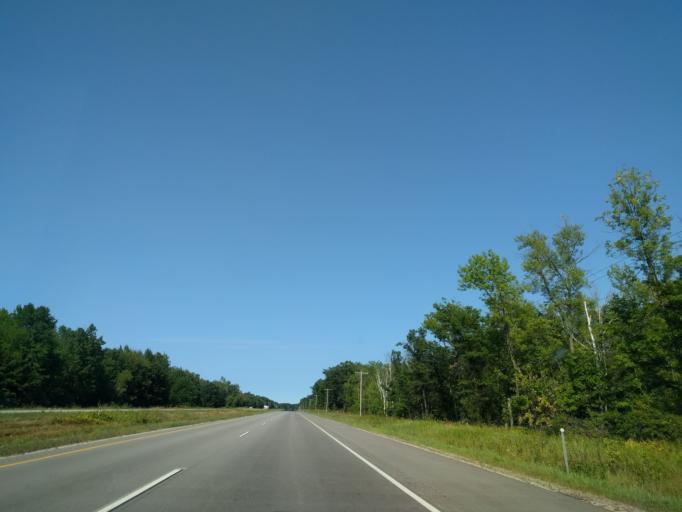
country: US
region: Wisconsin
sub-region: Oconto County
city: Oconto
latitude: 44.8393
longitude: -87.9140
